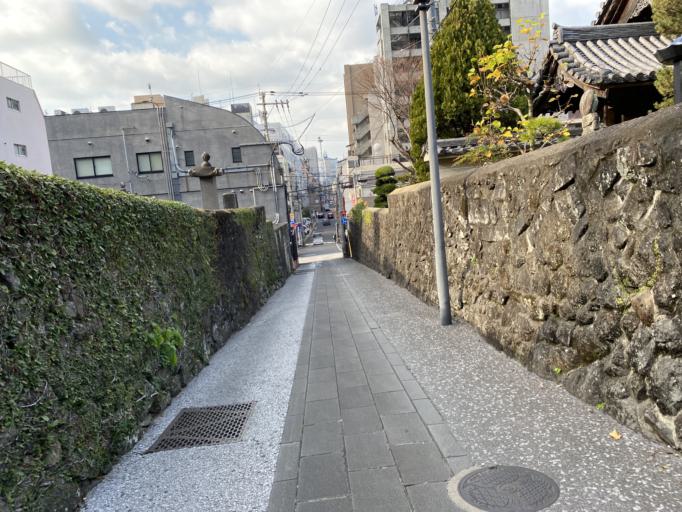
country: JP
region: Nagasaki
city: Nagasaki-shi
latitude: 32.7452
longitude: 129.8821
